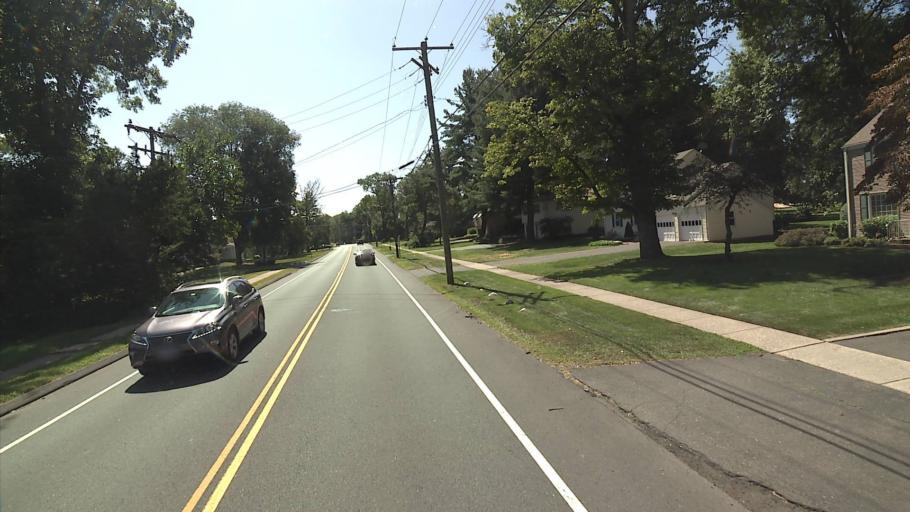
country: US
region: Connecticut
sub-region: Hartford County
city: West Hartford
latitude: 41.8032
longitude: -72.7507
